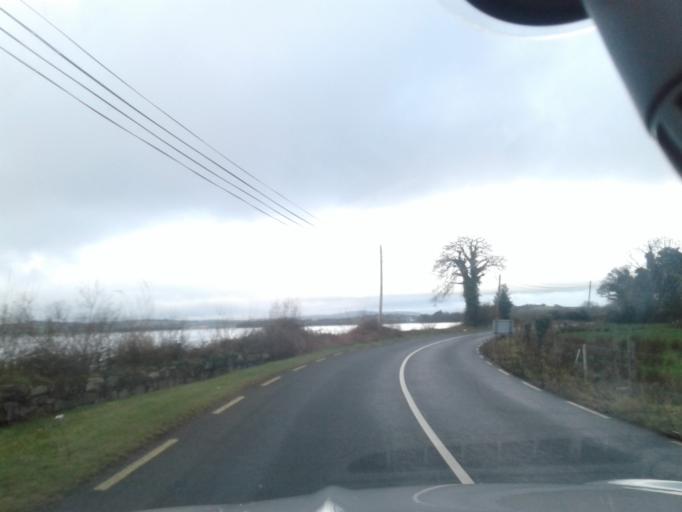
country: IE
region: Ulster
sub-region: County Donegal
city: Ramelton
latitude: 55.0835
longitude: -7.5774
